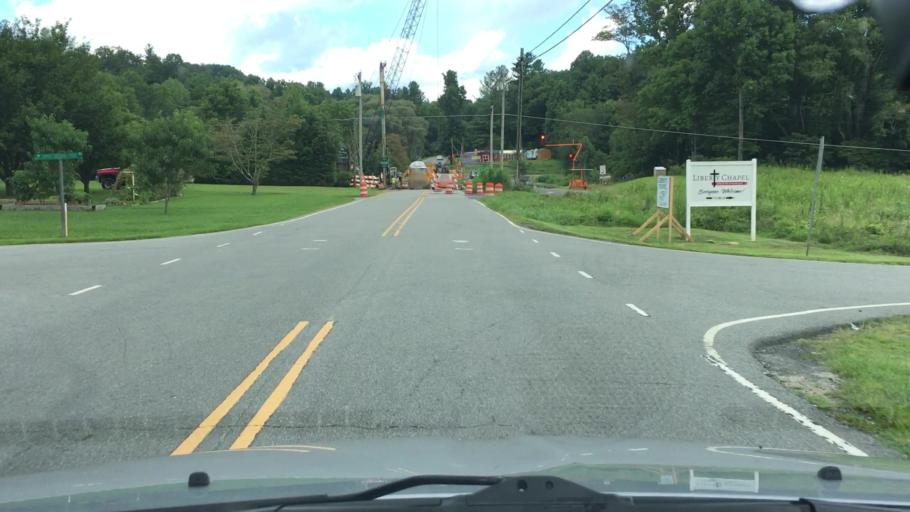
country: US
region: North Carolina
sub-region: Yancey County
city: Burnsville
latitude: 35.8550
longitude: -82.1995
